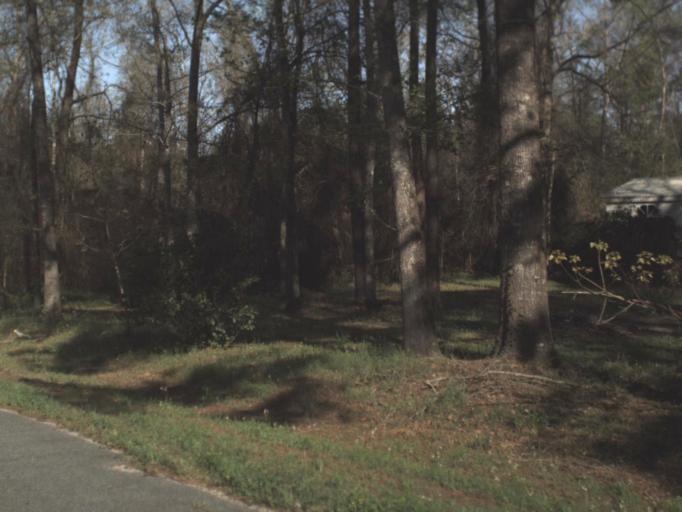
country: US
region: Florida
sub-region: Jackson County
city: Malone
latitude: 30.9762
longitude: -85.0155
